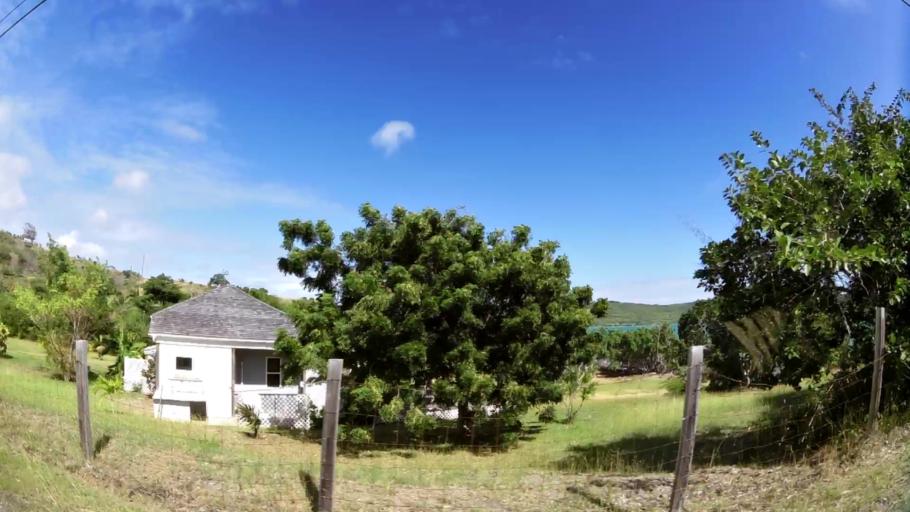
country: AG
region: Saint Paul
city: Falmouth
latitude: 17.0301
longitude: -61.7411
